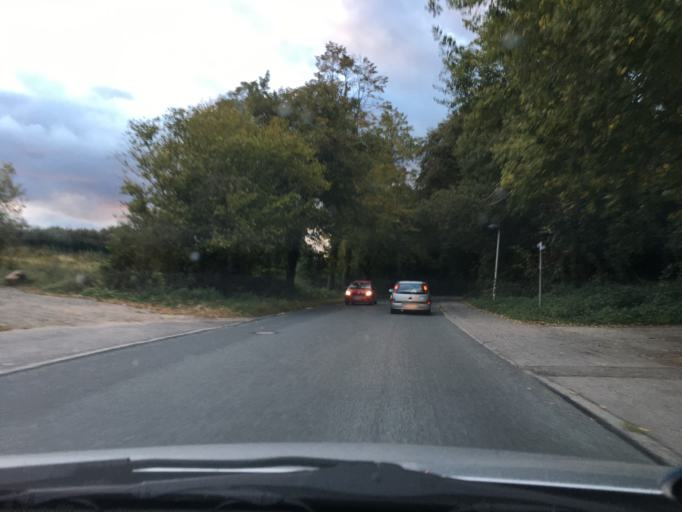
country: DE
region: Schleswig-Holstein
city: Altenholz
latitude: 54.3842
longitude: 10.1527
